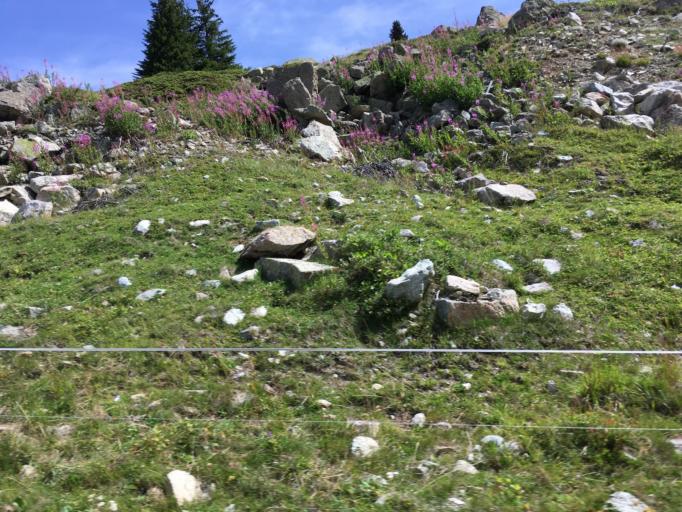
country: CH
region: Grisons
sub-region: Maloja District
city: Silvaplana
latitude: 46.4656
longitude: 9.7079
